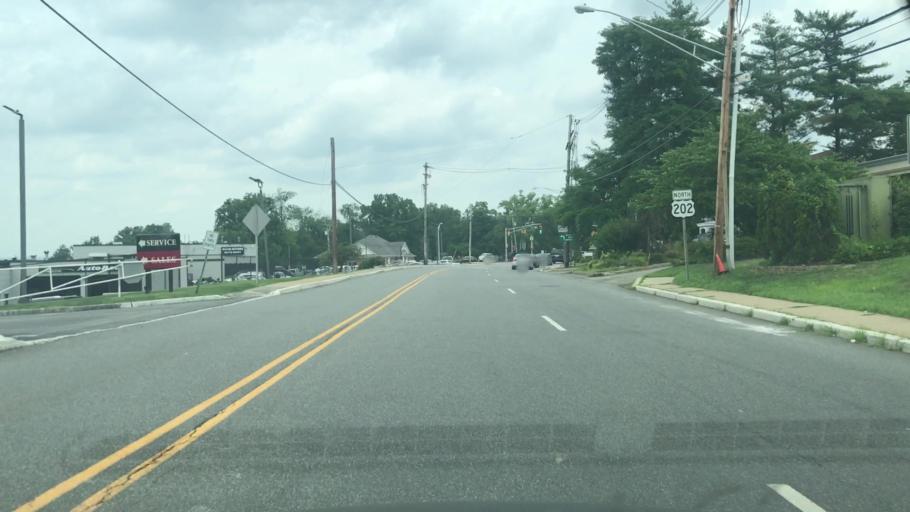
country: US
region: New Jersey
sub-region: Passaic County
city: Wayne
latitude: 40.9475
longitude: -74.2739
